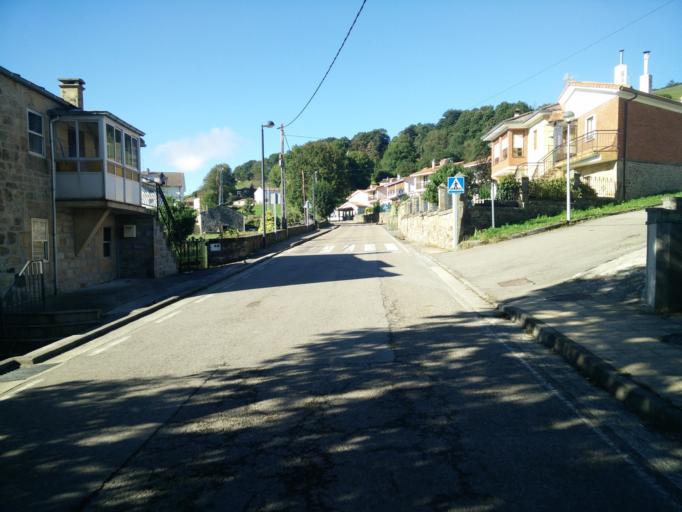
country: ES
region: Cantabria
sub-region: Provincia de Cantabria
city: San Pedro del Romeral
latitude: 43.1173
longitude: -3.8159
